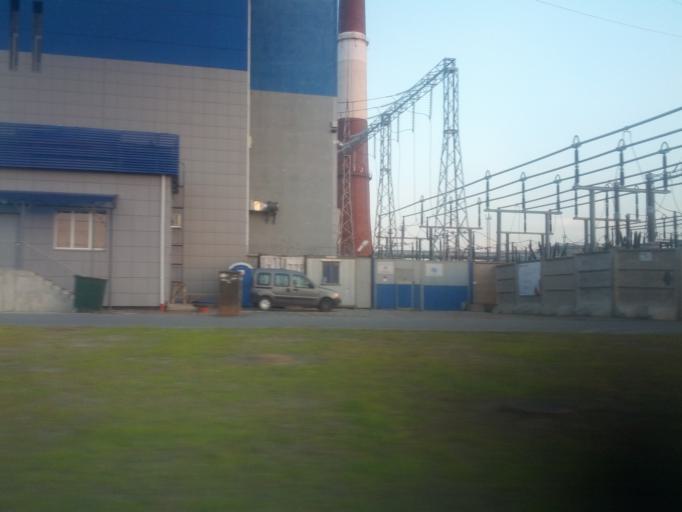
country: RU
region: St.-Petersburg
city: Staraya Derevnya
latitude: 59.9967
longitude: 30.2430
